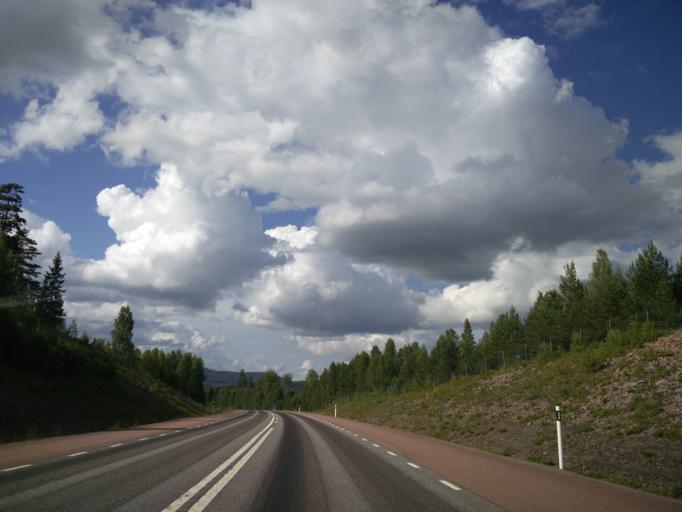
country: SE
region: Vaermland
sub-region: Torsby Kommun
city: Torsby
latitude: 60.1963
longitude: 13.0223
